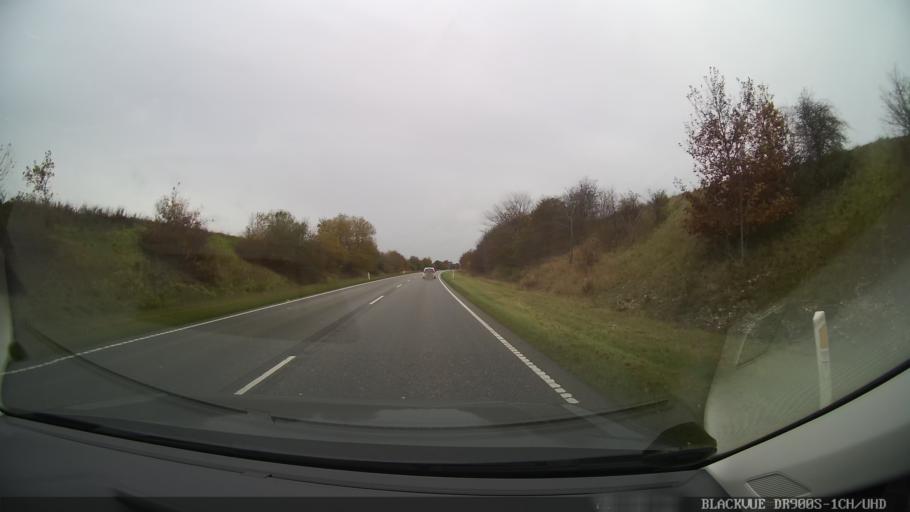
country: DK
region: North Denmark
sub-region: Morso Kommune
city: Nykobing Mors
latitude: 56.8264
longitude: 8.7252
